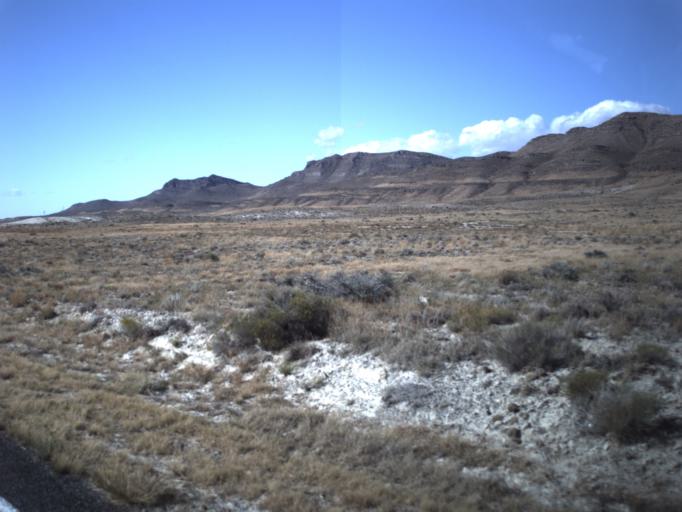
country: US
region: Utah
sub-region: Beaver County
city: Milford
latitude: 38.8737
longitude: -112.8344
